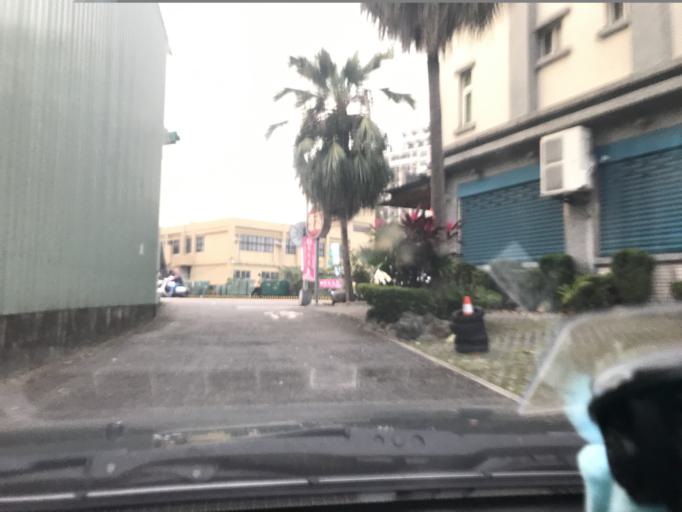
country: TW
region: Taiwan
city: Daxi
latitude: 24.8581
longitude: 121.2177
